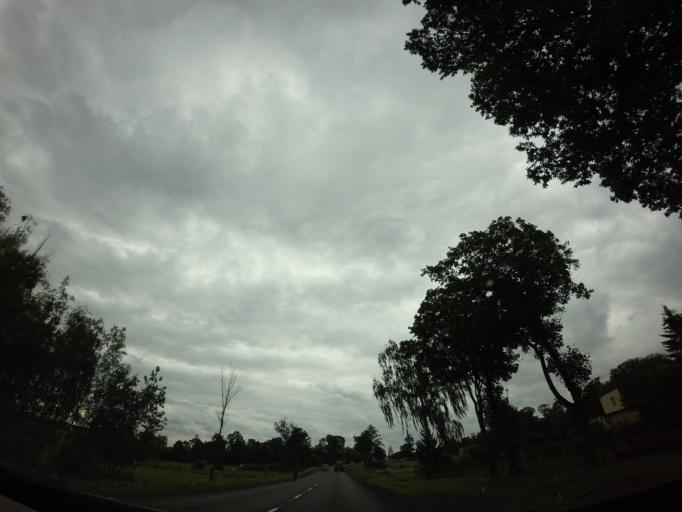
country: PL
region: Masovian Voivodeship
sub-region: Powiat makowski
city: Karniewo
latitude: 52.8378
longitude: 20.9811
